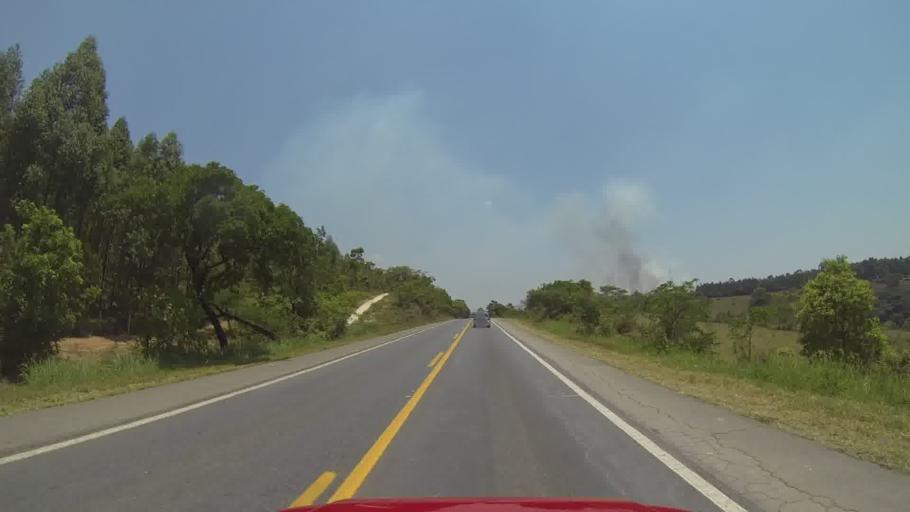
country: BR
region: Minas Gerais
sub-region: Itapecerica
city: Itapecerica
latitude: -20.3426
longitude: -45.2600
